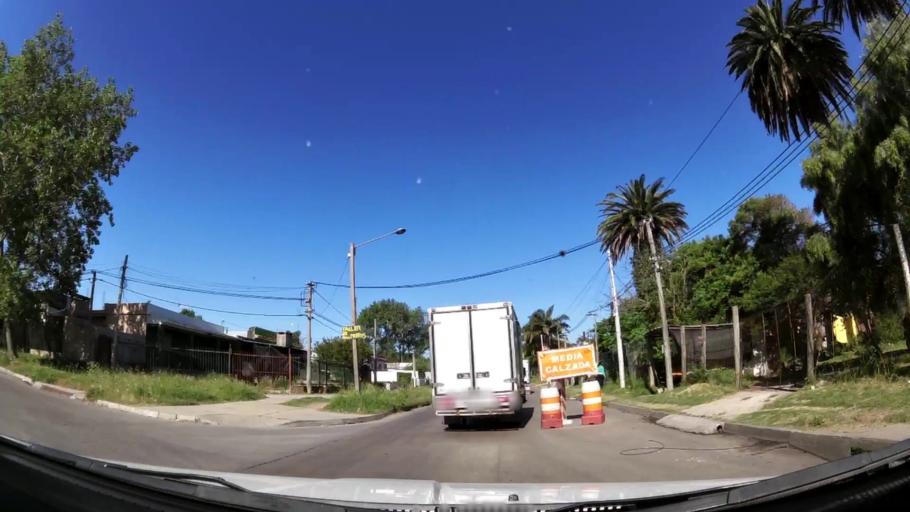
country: UY
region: Montevideo
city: Montevideo
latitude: -34.8332
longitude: -56.1460
